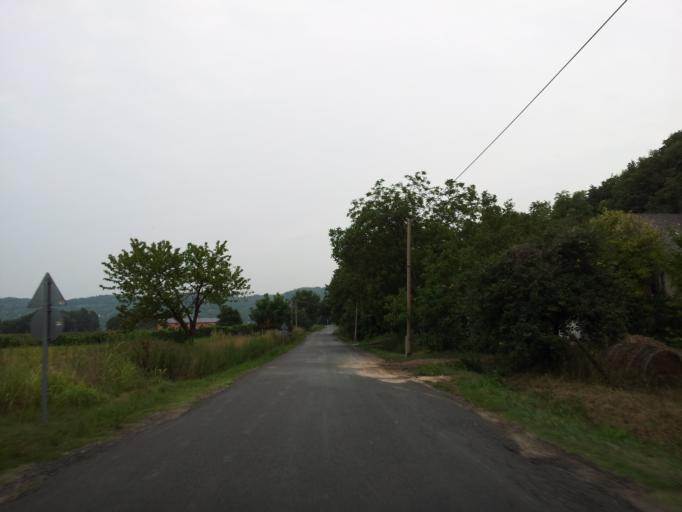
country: HU
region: Tolna
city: Szentgalpuszta
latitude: 46.3857
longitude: 18.6642
